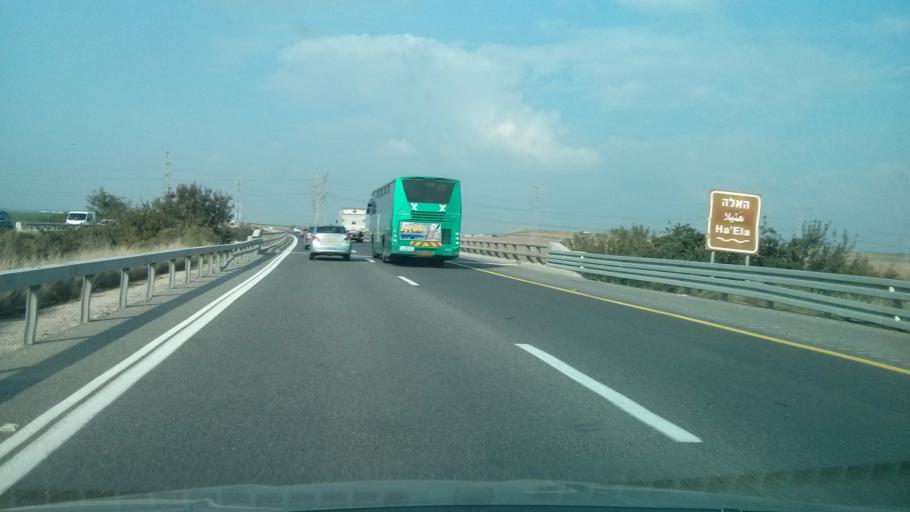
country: IL
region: Central District
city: Bene 'Ayish
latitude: 31.7074
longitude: 34.8200
